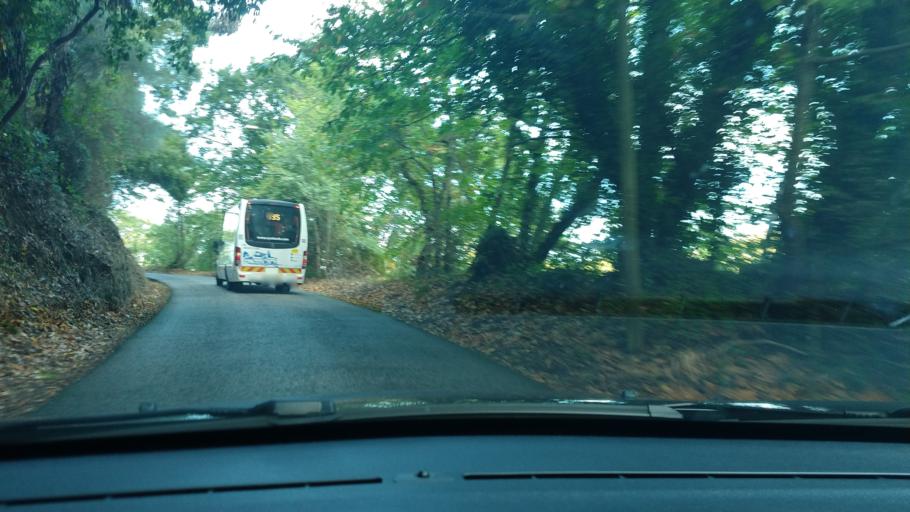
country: PT
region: Lisbon
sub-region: Sintra
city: Colares
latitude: 38.7975
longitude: -9.4388
